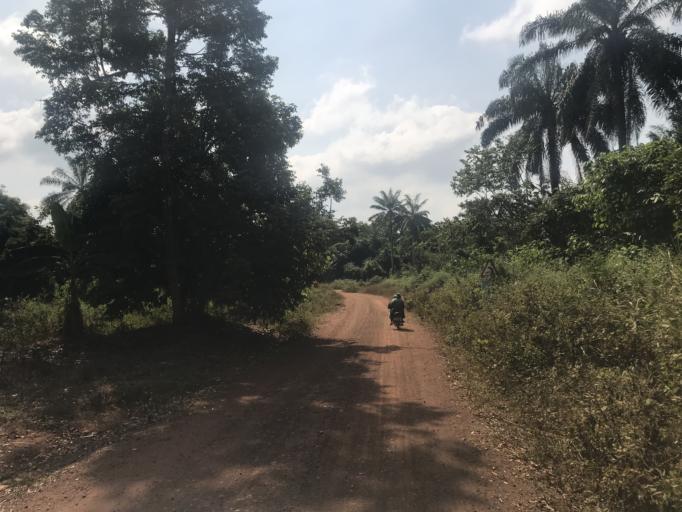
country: NG
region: Osun
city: Ibokun
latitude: 7.8068
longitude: 4.6474
